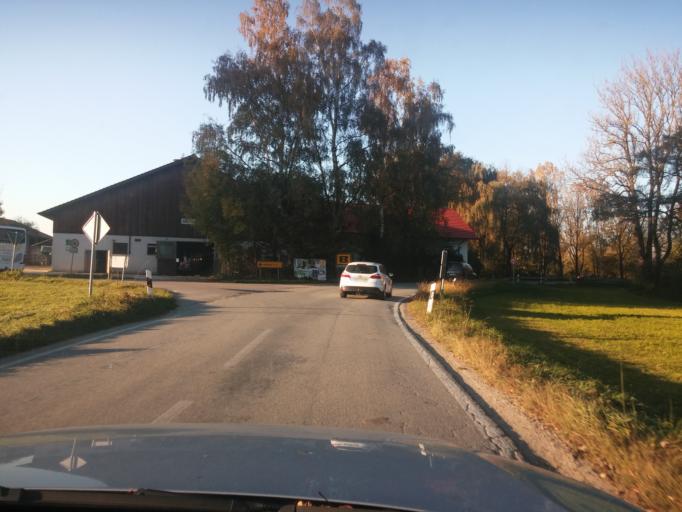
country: DE
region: Bavaria
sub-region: Upper Bavaria
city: Dorfen
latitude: 48.2579
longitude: 12.1331
